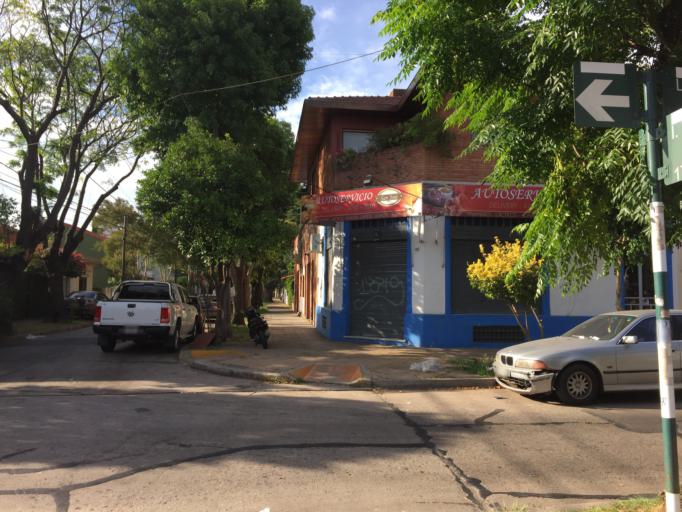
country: AR
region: Buenos Aires
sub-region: Partido de Vicente Lopez
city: Olivos
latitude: -34.5293
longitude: -58.4993
